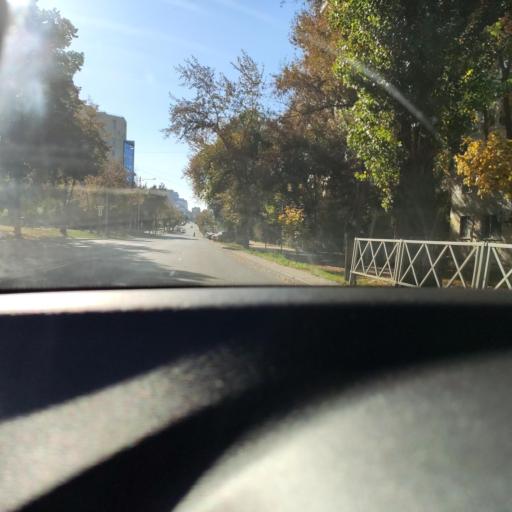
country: RU
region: Samara
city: Samara
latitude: 53.2082
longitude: 50.1237
